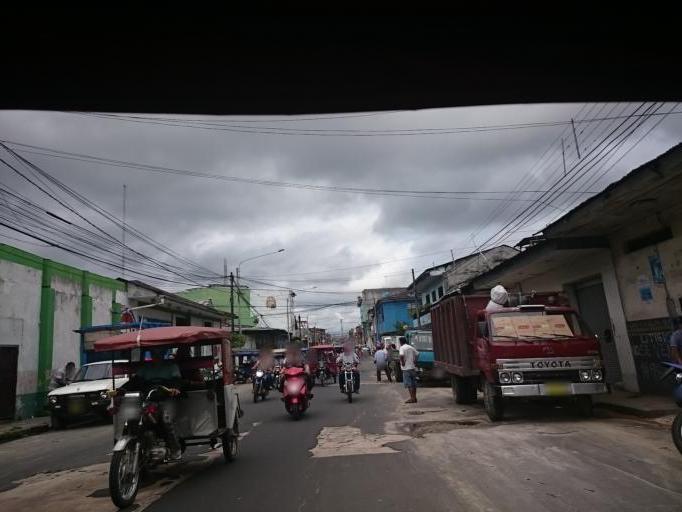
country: PE
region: Loreto
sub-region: Provincia de Maynas
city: Iquitos
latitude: -3.7438
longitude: -73.2423
